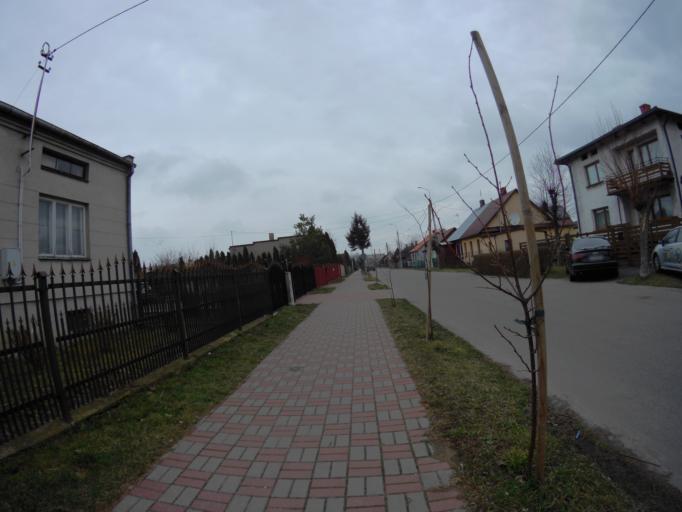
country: PL
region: Lublin Voivodeship
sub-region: Powiat bialski
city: Terespol
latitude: 52.0765
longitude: 23.6156
